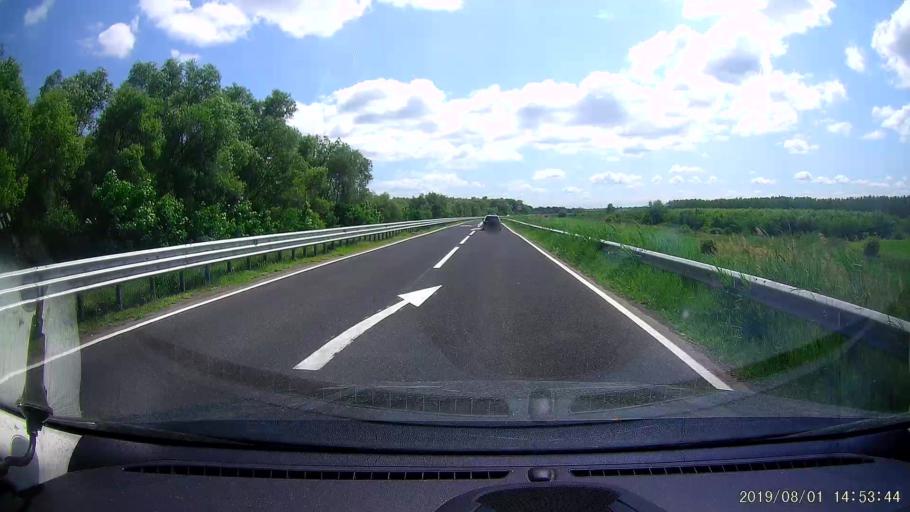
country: RO
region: Braila
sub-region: Municipiul Braila
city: Braila
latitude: 45.3296
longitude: 27.9991
